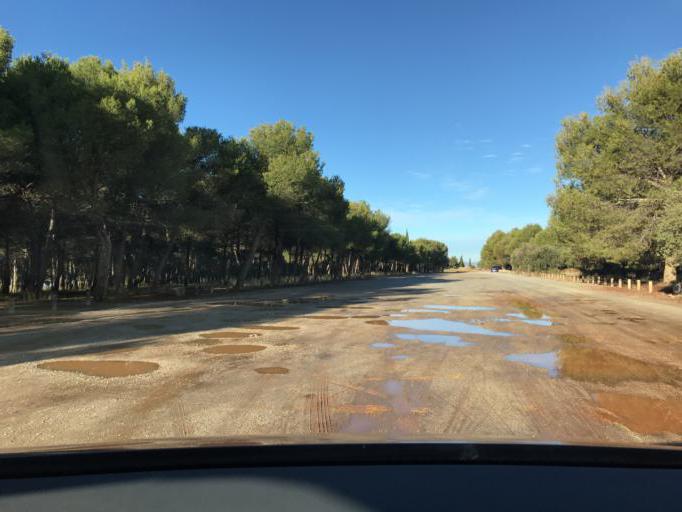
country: ES
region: Andalusia
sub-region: Provincia de Granada
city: Cenes de la Vega
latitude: 37.1748
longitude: -3.5568
